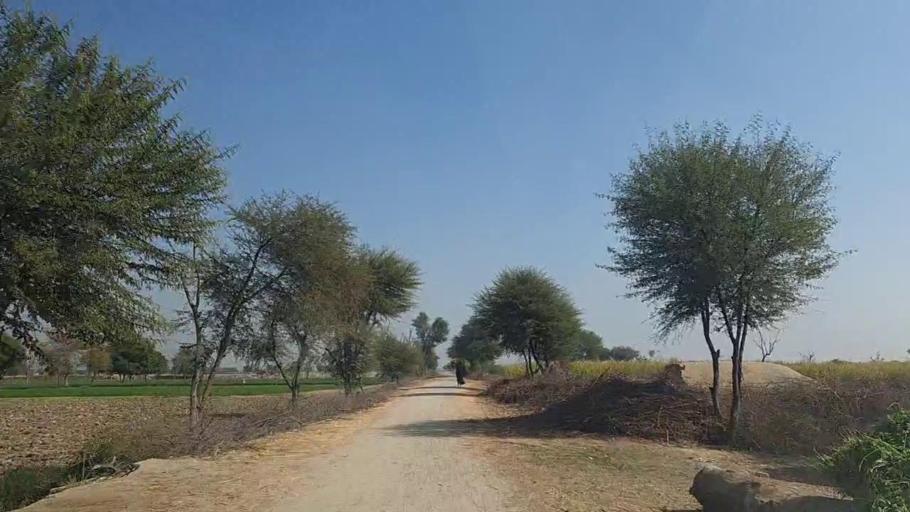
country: PK
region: Sindh
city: Shahpur Chakar
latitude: 26.2026
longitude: 68.5806
